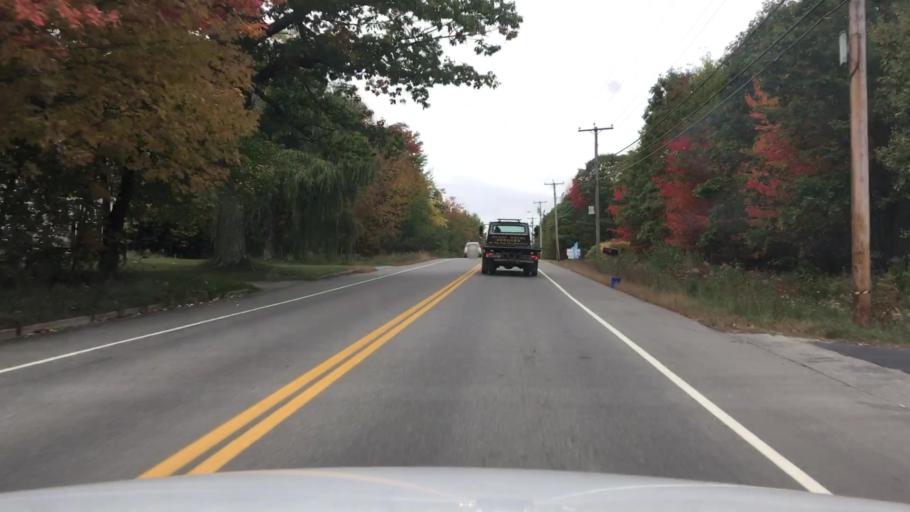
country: US
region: Maine
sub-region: Kennebec County
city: Oakland
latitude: 44.5545
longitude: -69.7349
